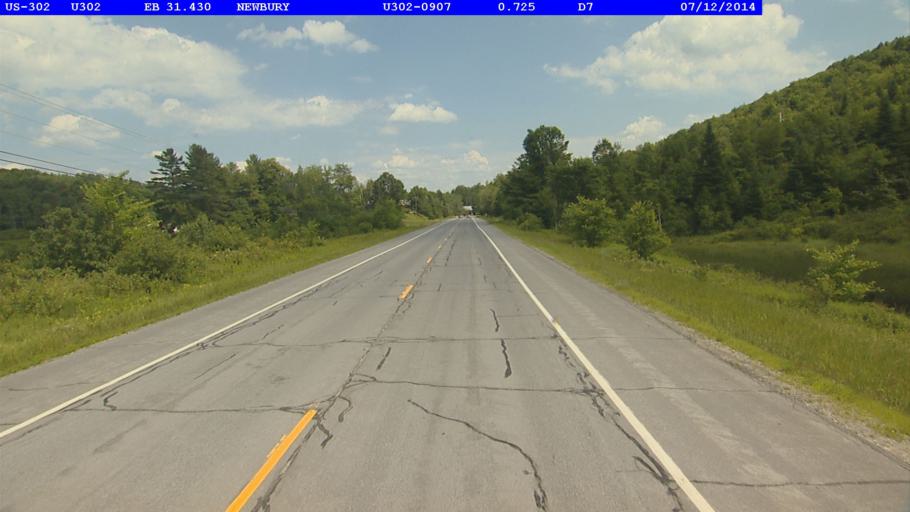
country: US
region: New Hampshire
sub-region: Grafton County
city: Woodsville
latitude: 44.1708
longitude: -72.1050
